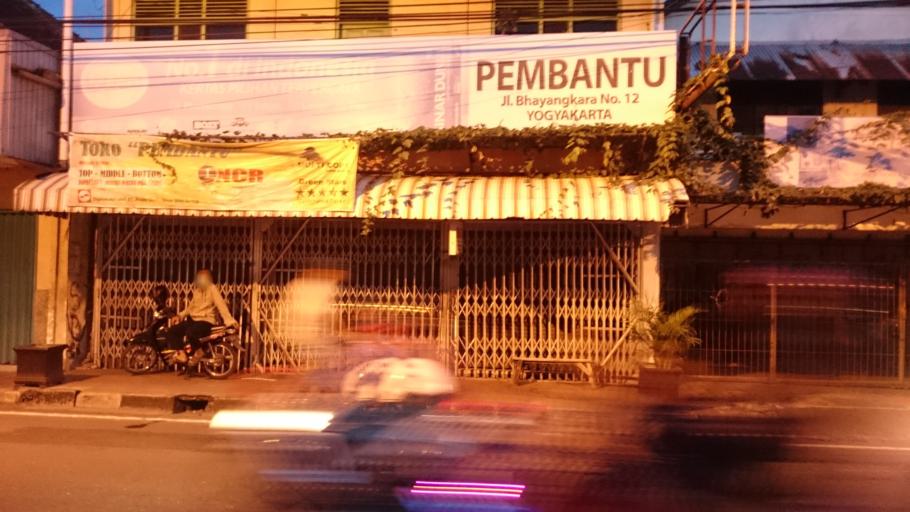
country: ID
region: Daerah Istimewa Yogyakarta
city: Yogyakarta
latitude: -7.8001
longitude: 110.3620
